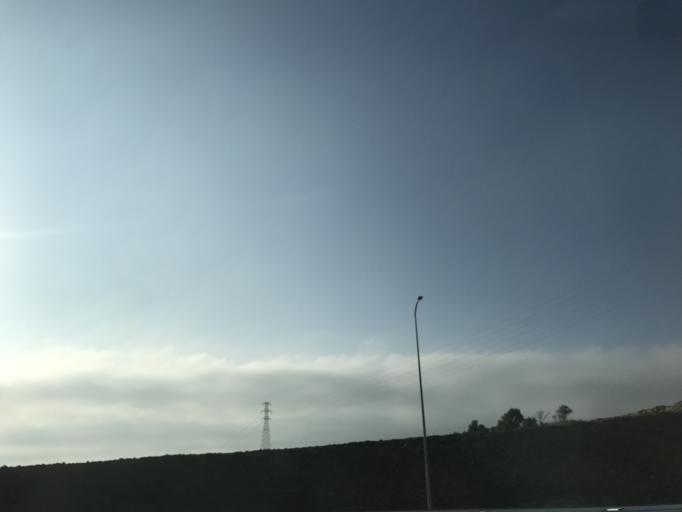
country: TR
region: Balikesir
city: Susurluk
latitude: 39.9658
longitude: 28.1583
